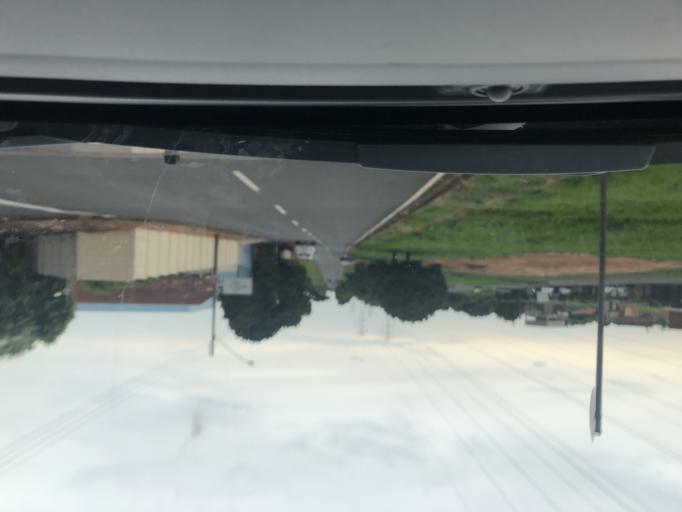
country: BR
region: Sao Paulo
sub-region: Sao Jose Do Rio Preto
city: Sao Jose do Rio Preto
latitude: -20.8444
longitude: -49.3844
